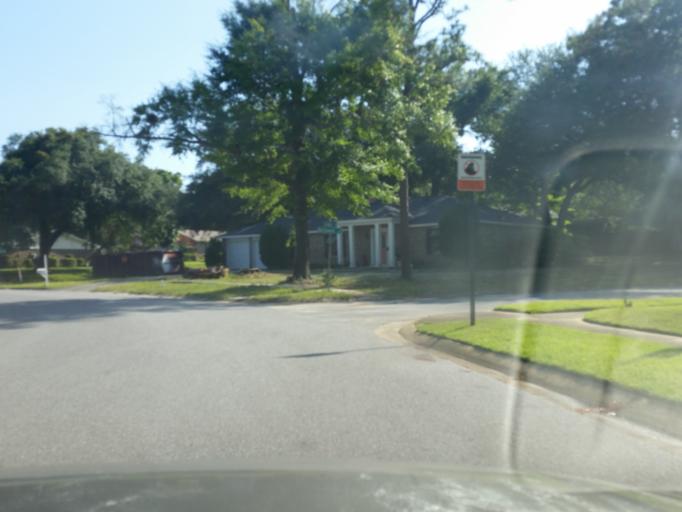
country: US
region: Florida
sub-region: Escambia County
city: Ferry Pass
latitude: 30.5222
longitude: -87.1810
